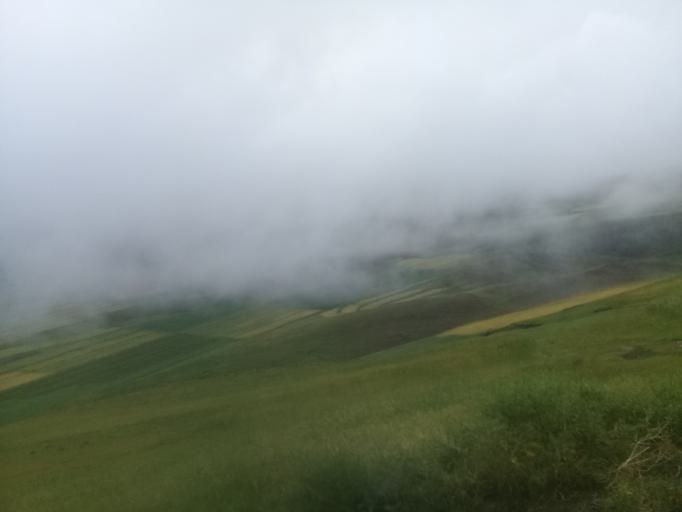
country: LS
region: Mokhotlong
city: Mokhotlong
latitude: -29.3828
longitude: 28.9808
